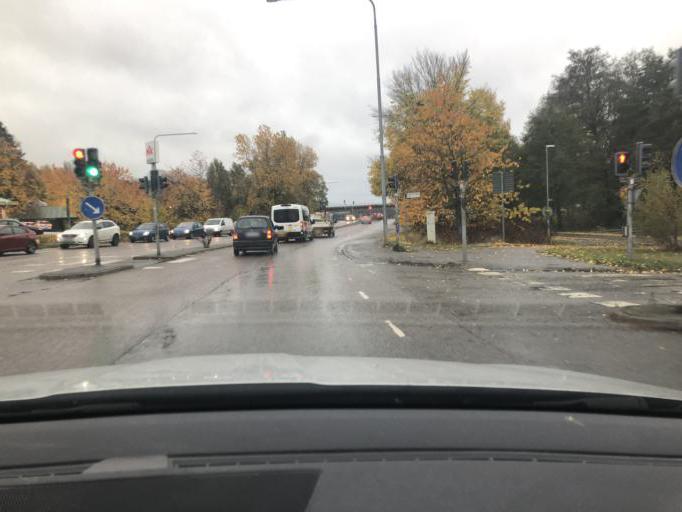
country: SE
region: Stockholm
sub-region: Botkyrka Kommun
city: Fittja
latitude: 59.2521
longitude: 17.8759
